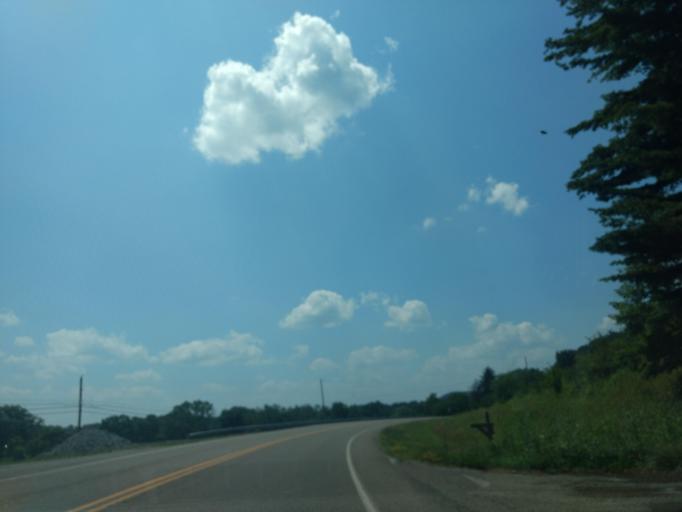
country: US
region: Pennsylvania
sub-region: Butler County
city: Zelienople
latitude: 40.8124
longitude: -80.1058
